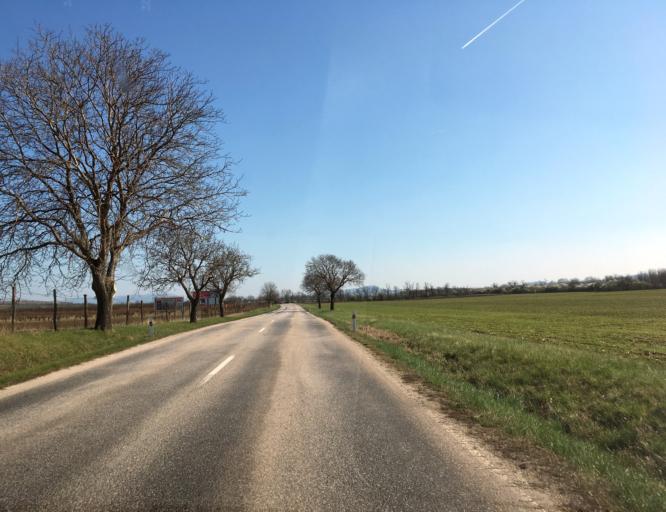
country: HU
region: Komarom-Esztergom
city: Nyergesujfalu
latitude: 47.8367
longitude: 18.5413
